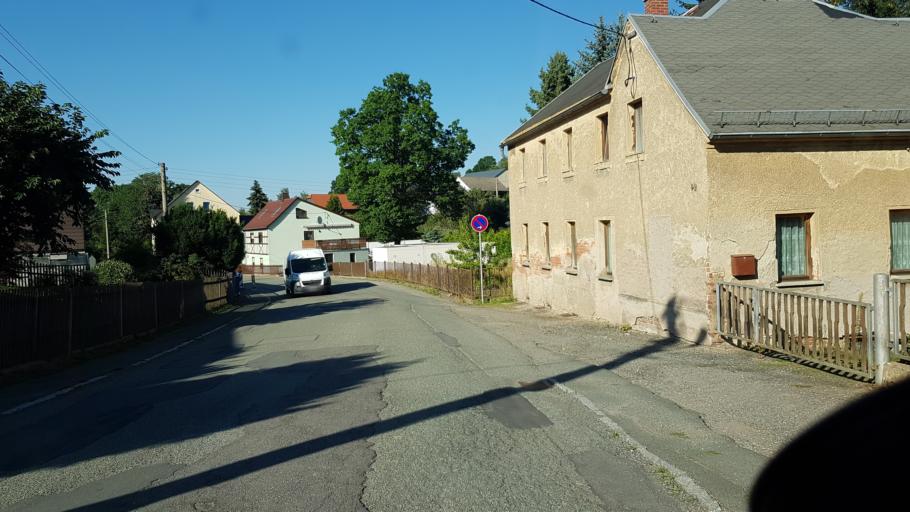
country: DE
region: Saxony
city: Hirschfeld
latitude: 50.6530
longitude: 12.4395
